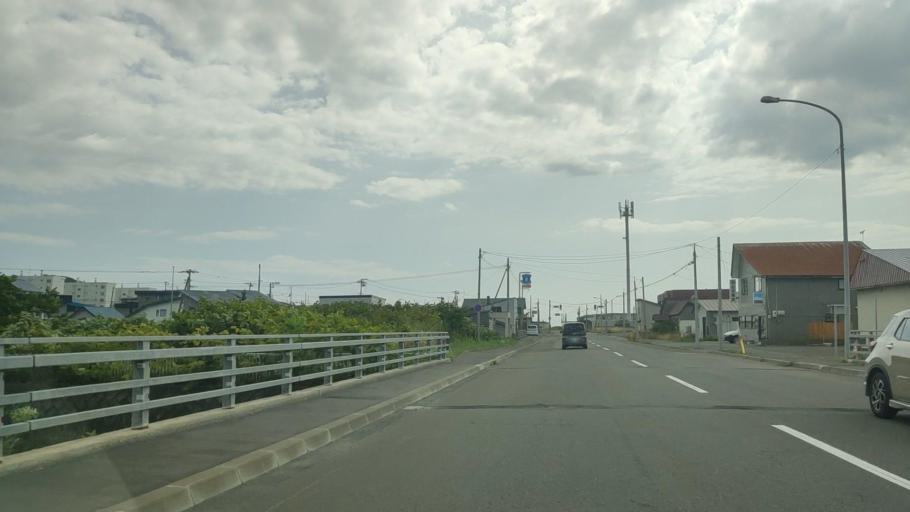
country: JP
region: Hokkaido
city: Rumoi
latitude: 44.1530
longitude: 141.6559
